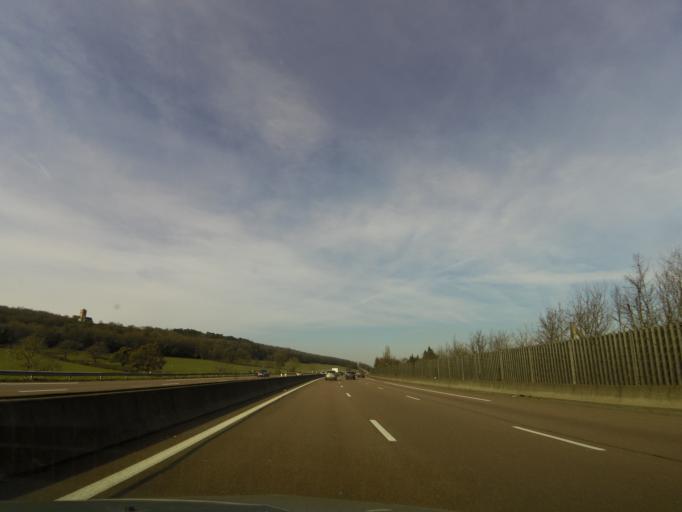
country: FR
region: Bourgogne
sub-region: Departement de Saone-et-Loire
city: Sennecey-le-Grand
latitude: 46.6350
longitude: 4.8597
